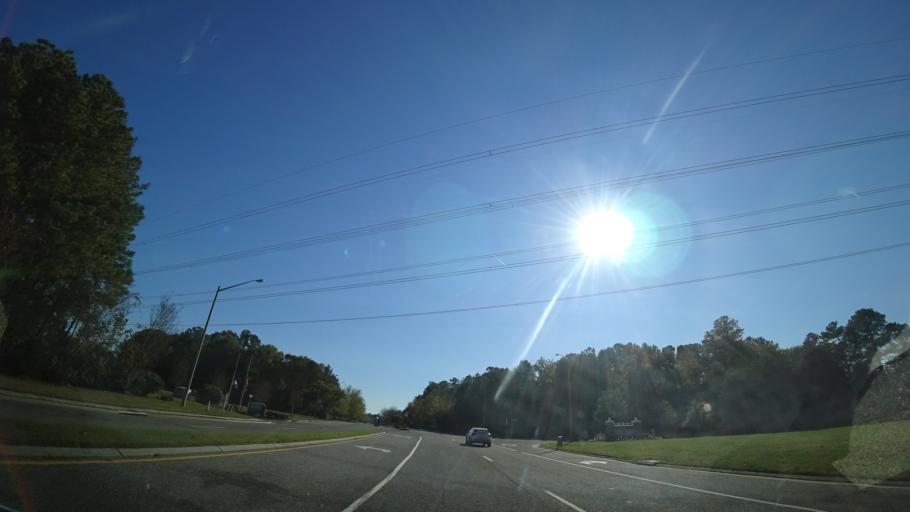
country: US
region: Virginia
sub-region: City of Newport News
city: Newport News
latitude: 36.8911
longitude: -76.4375
